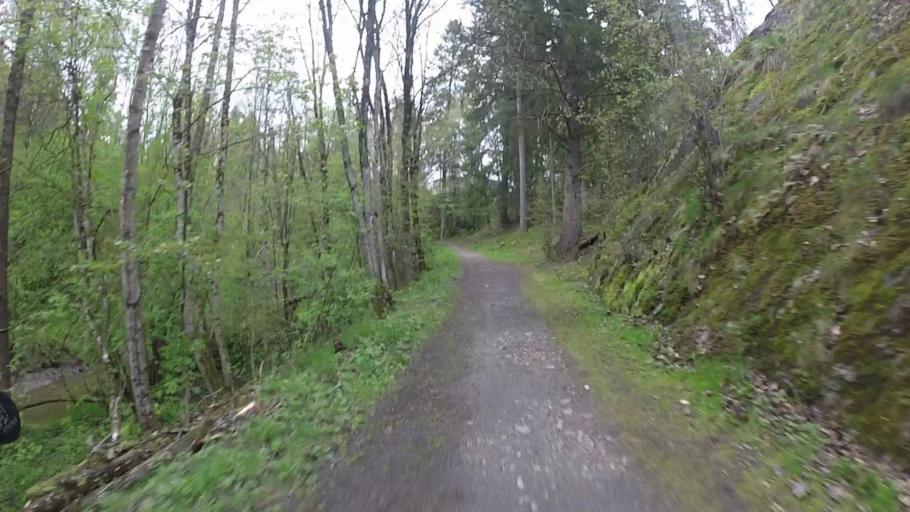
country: SE
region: Vaestra Goetaland
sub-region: Trollhattan
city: Trollhattan
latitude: 58.2609
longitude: 12.2543
